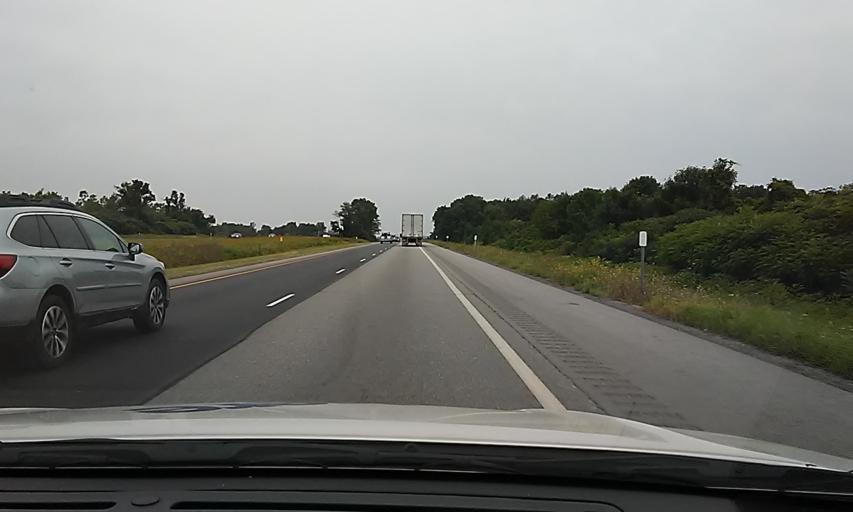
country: US
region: New York
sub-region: Genesee County
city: Le Roy
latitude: 43.0266
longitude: -78.0542
